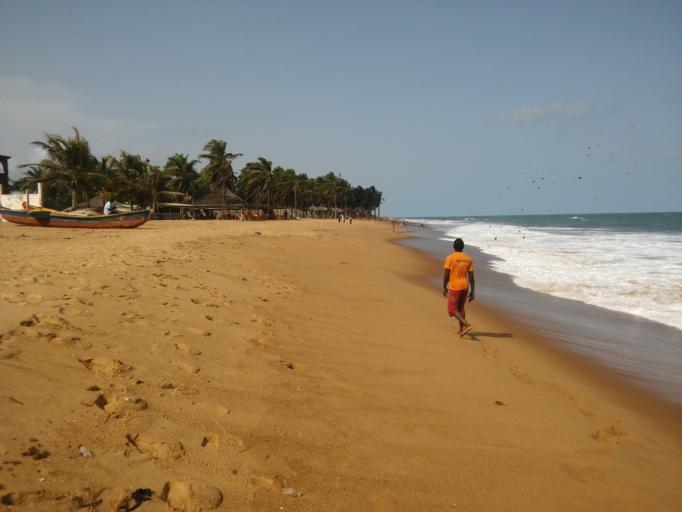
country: TG
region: Maritime
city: Lome
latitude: 6.1654
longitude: 1.3441
